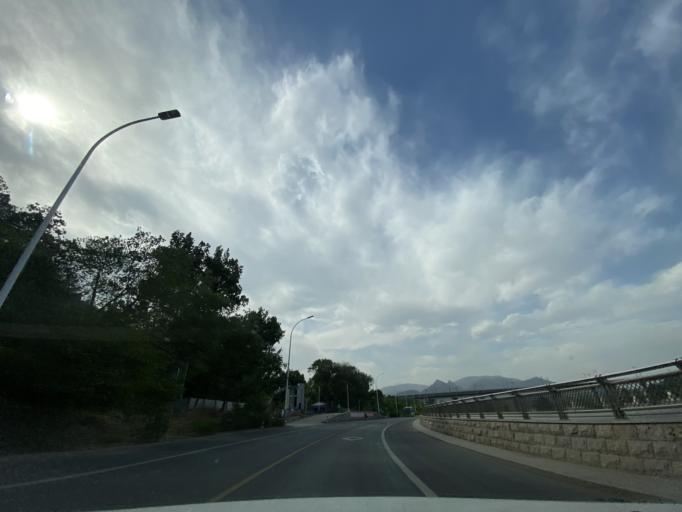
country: CN
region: Beijing
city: Chengzi
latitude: 39.9622
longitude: 116.0885
